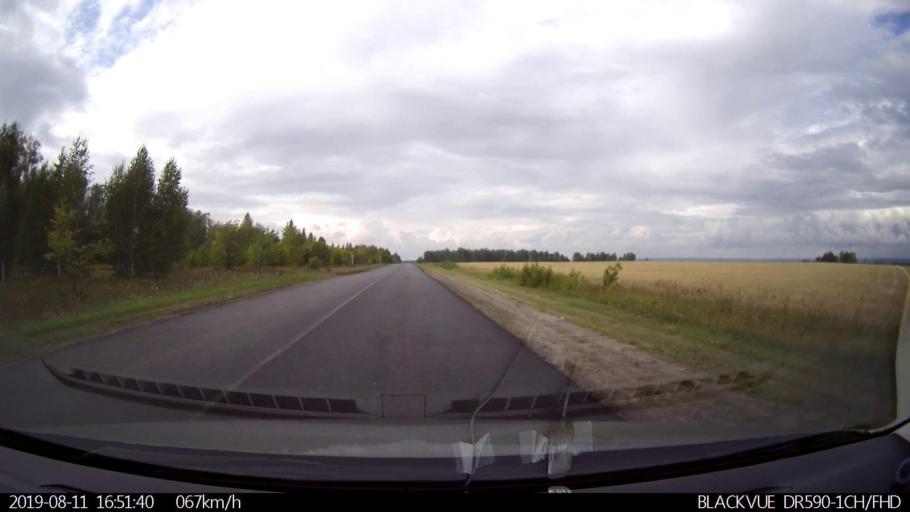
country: RU
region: Ulyanovsk
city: Mayna
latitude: 54.2395
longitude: 47.6763
